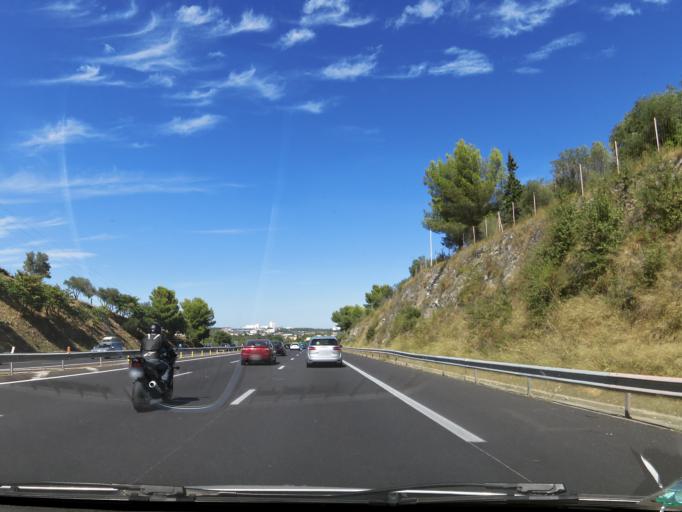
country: FR
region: Languedoc-Roussillon
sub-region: Departement du Gard
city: Milhaud
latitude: 43.7953
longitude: 4.3061
